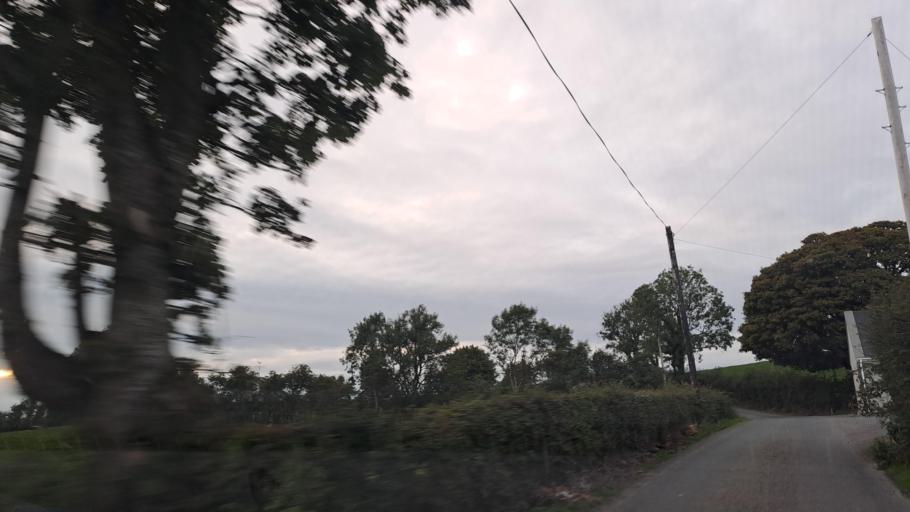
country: IE
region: Ulster
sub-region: An Cabhan
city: Kingscourt
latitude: 53.9792
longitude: -6.8561
